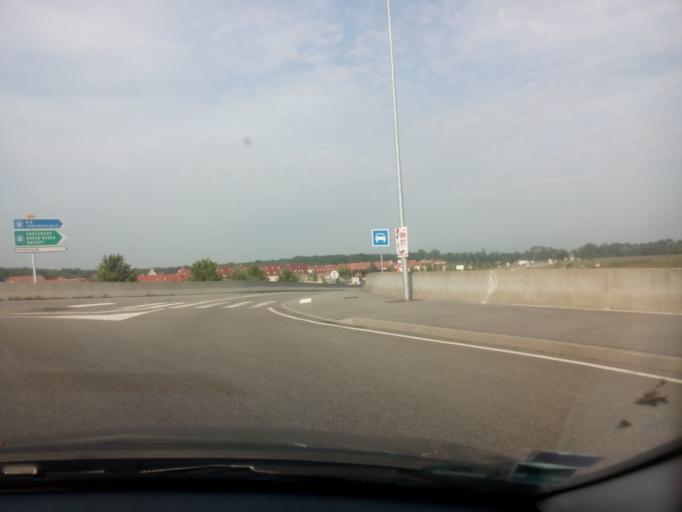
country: FR
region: Alsace
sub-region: Departement du Bas-Rhin
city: Roppenheim
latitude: 48.8357
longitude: 8.0837
